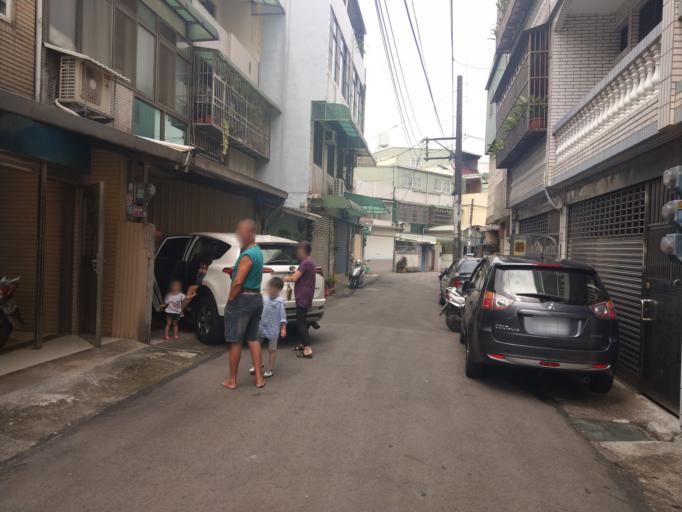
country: TW
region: Taiwan
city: Taoyuan City
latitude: 24.9495
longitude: 121.2483
